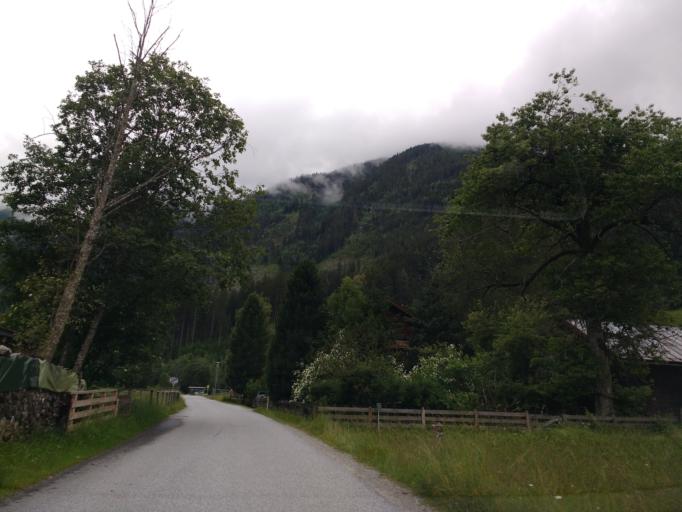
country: AT
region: Salzburg
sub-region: Politischer Bezirk Zell am See
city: Wald im Pinzgau
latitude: 47.2324
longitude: 12.2481
